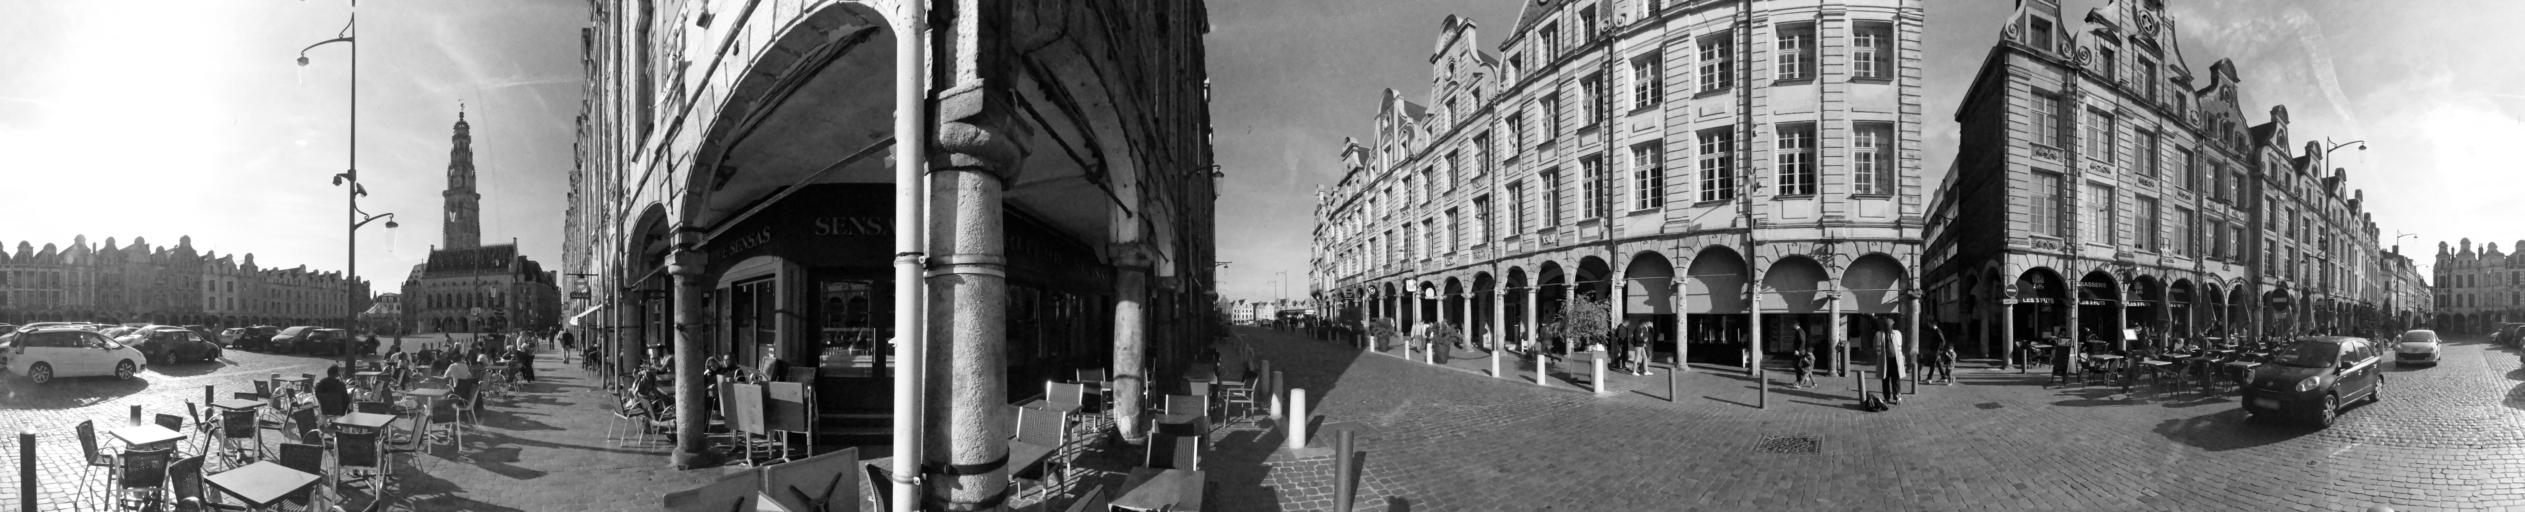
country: FR
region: Nord-Pas-de-Calais
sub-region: Departement du Pas-de-Calais
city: Arras
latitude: 50.2908
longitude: 2.7785
